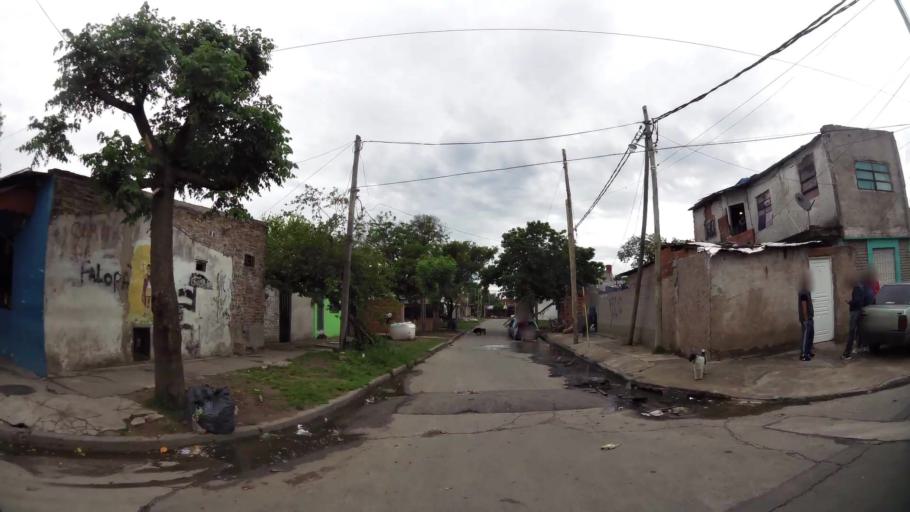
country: AR
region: Buenos Aires
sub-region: Partido de Lomas de Zamora
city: Lomas de Zamora
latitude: -34.7398
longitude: -58.3595
